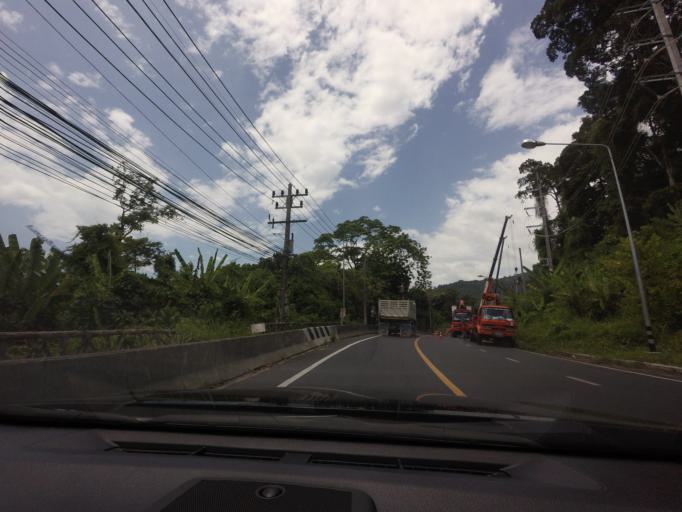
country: TH
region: Phangnga
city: Ban Khao Lak
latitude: 8.6350
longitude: 98.2457
